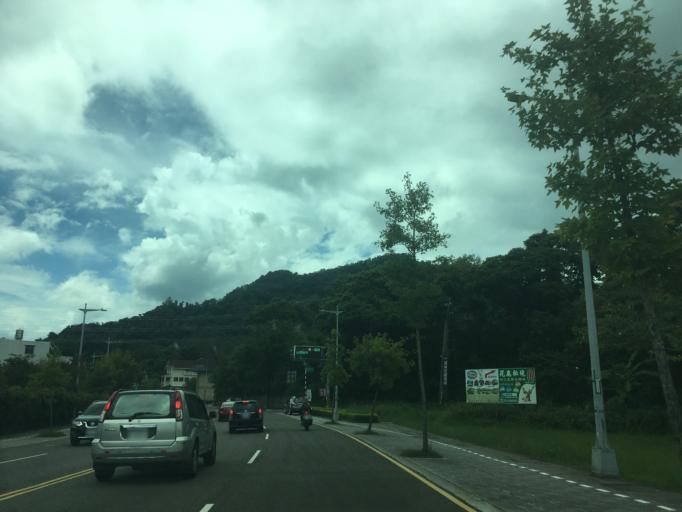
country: TW
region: Taiwan
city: Daxi
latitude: 24.8420
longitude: 121.2880
